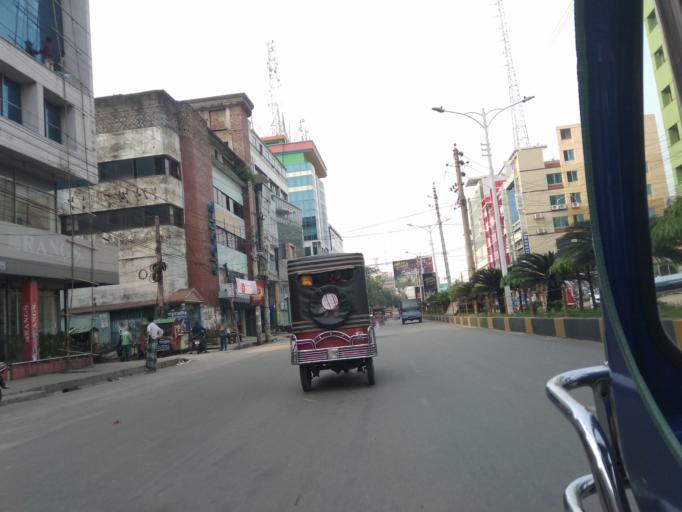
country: BD
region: Khulna
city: Khulna
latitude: 22.8196
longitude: 89.5530
